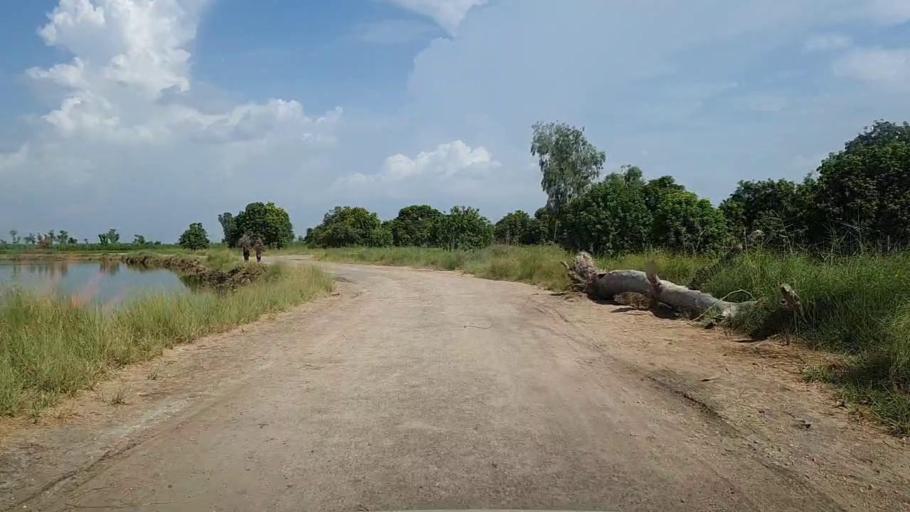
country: PK
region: Sindh
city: Bhiria
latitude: 26.9106
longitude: 68.2244
